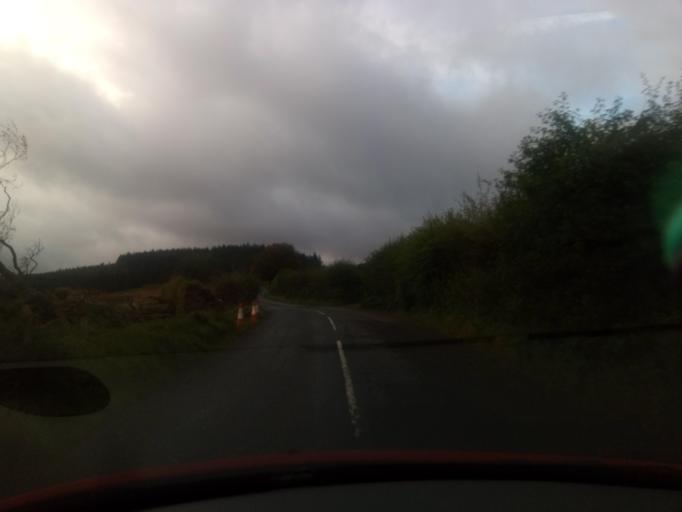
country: GB
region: Scotland
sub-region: The Scottish Borders
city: Hawick
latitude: 55.3421
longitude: -2.6516
